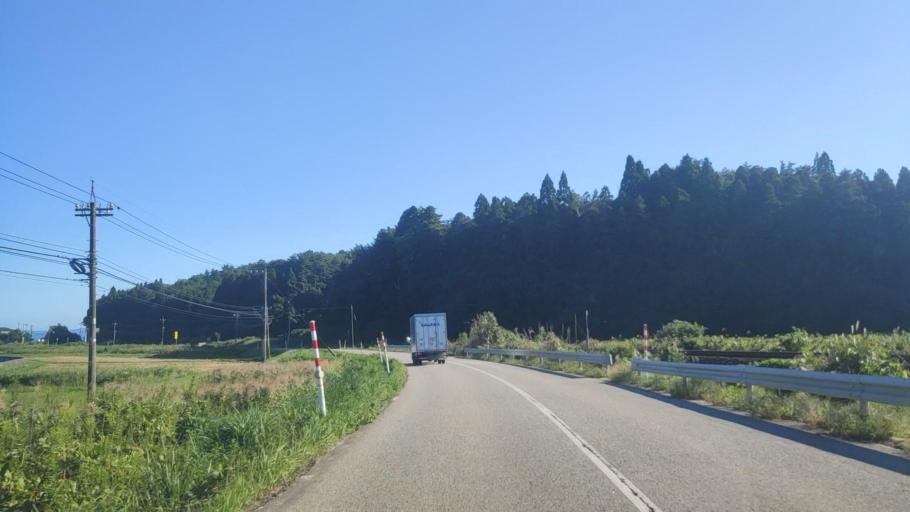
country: JP
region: Ishikawa
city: Nanao
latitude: 37.2020
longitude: 136.9060
